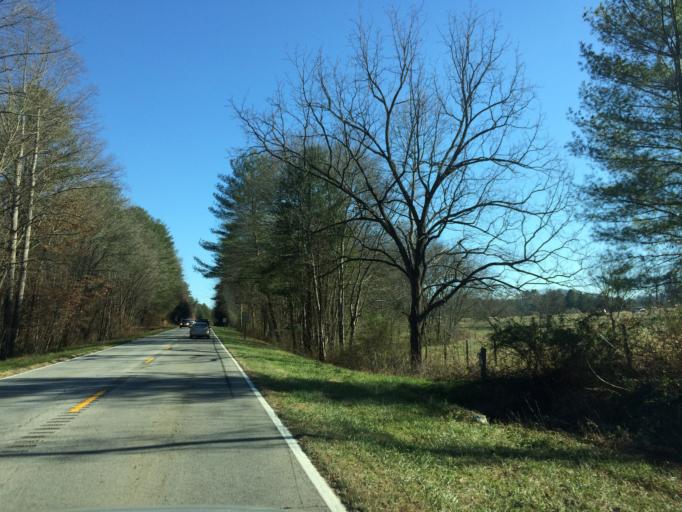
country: US
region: North Carolina
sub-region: Henderson County
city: Mountain Home
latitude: 35.3702
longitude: -82.5294
